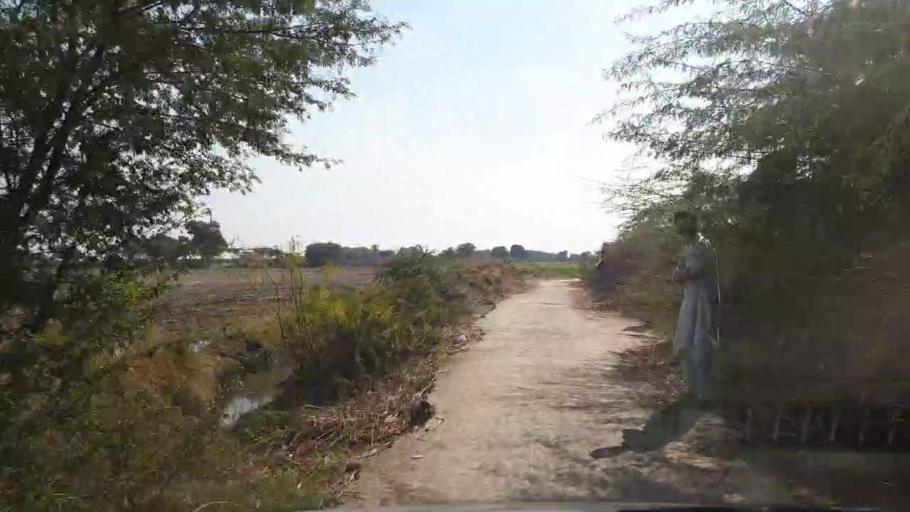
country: PK
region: Sindh
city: Chambar
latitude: 25.3253
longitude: 68.7908
